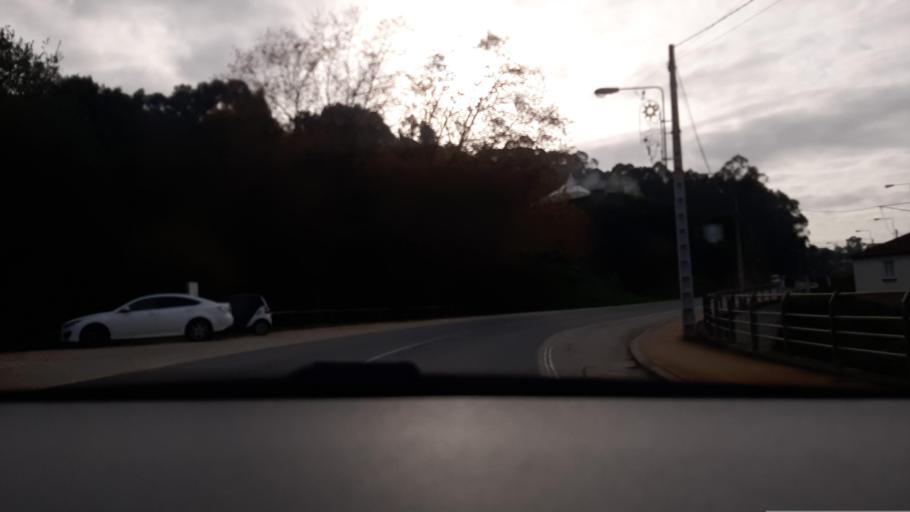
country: ES
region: Galicia
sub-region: Provincia de Pontevedra
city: Nigran
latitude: 42.1836
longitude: -8.7883
